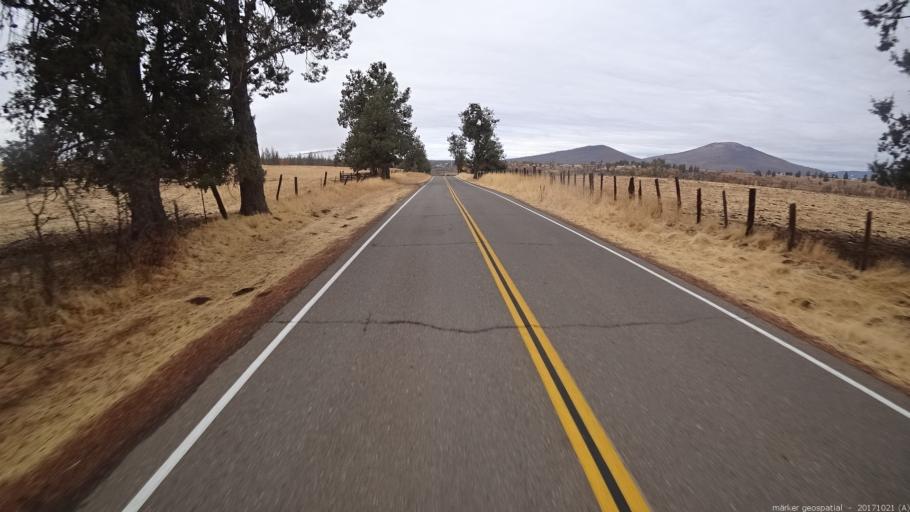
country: US
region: California
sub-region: Shasta County
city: Burney
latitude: 41.0139
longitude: -121.4184
